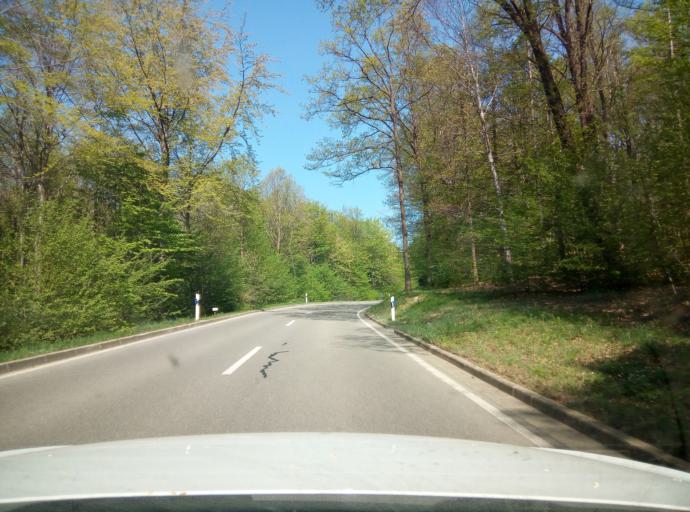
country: DE
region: Baden-Wuerttemberg
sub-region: Tuebingen Region
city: Kusterdingen
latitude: 48.5411
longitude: 9.1159
